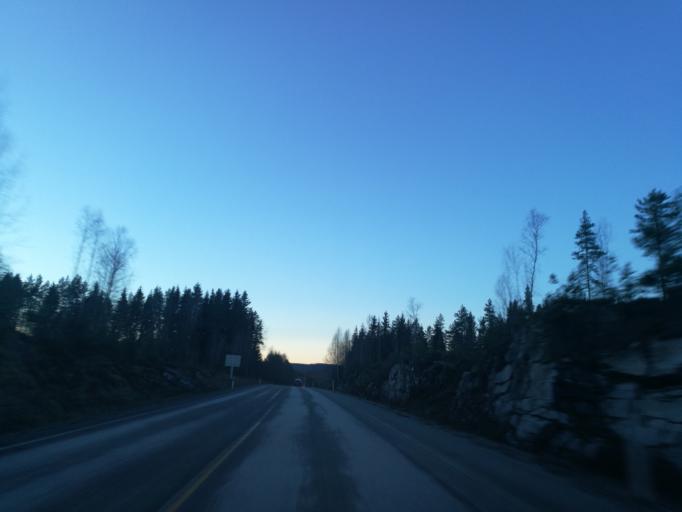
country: NO
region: Hedmark
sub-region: Eidskog
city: Skotterud
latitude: 59.9772
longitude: 12.1240
